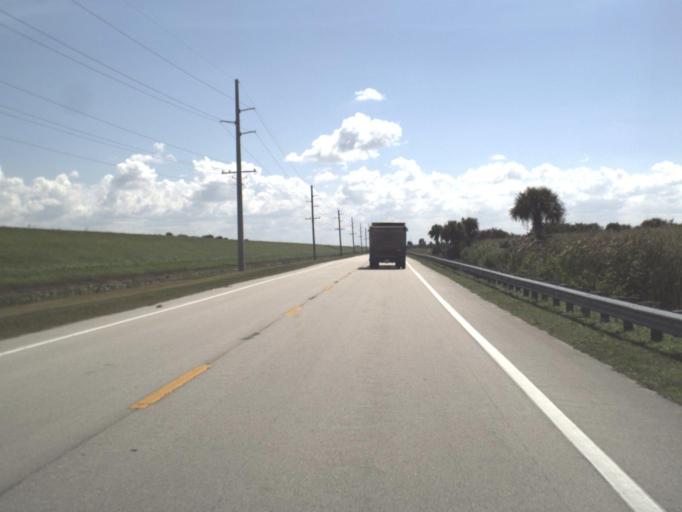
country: US
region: Florida
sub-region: Glades County
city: Moore Haven
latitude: 26.9100
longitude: -81.1224
